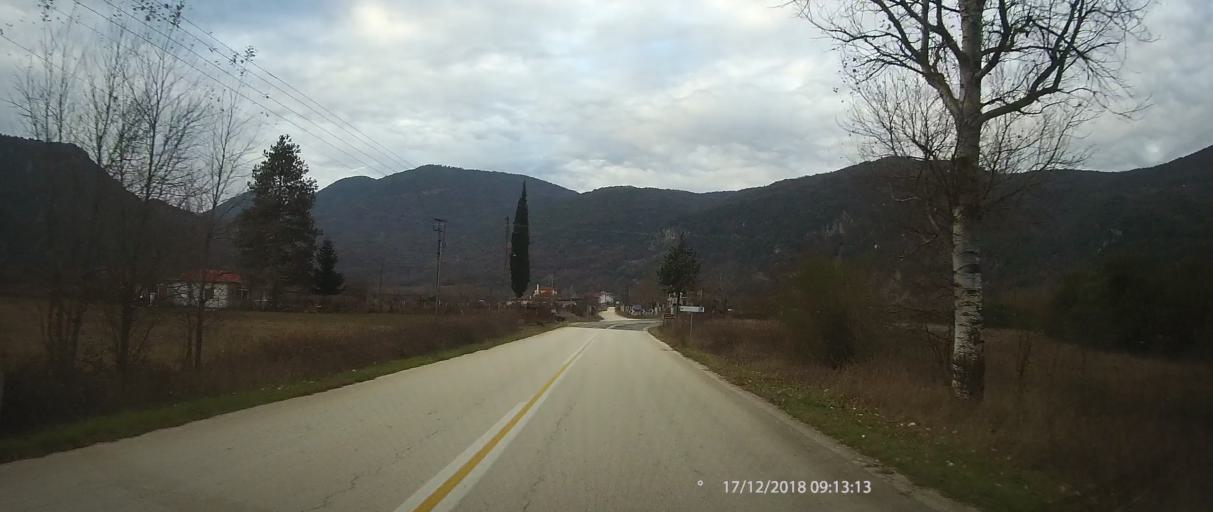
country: GR
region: Epirus
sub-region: Nomos Ioanninon
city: Kalpaki
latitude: 39.9743
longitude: 20.6610
